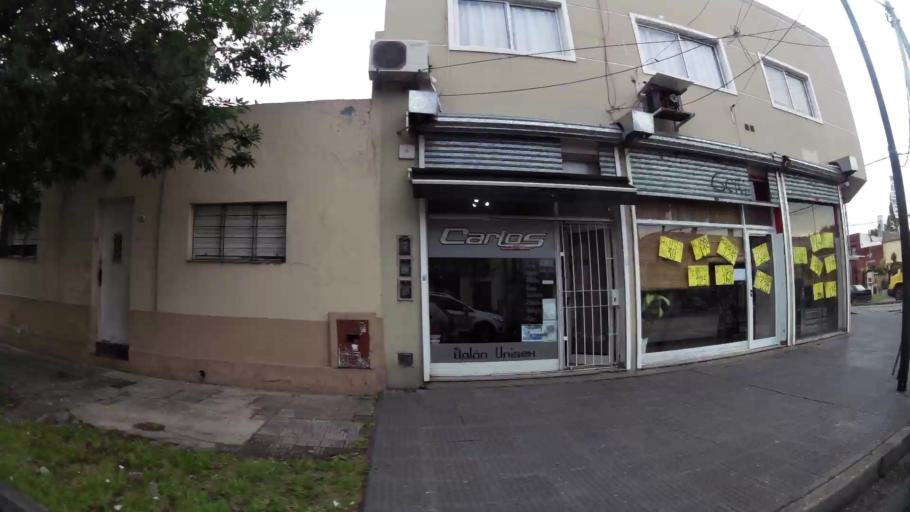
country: AR
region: Buenos Aires
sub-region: Partido de Lanus
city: Lanus
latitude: -34.6989
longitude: -58.3800
